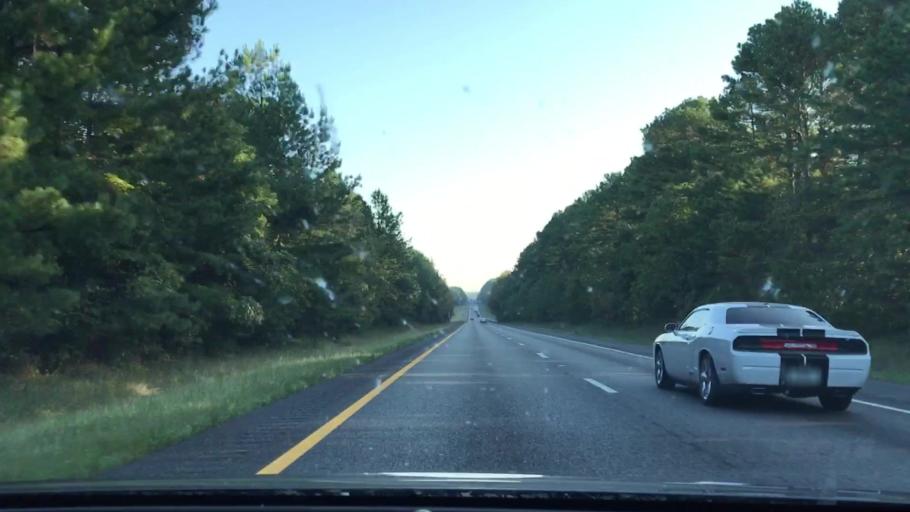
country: US
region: Tennessee
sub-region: Robertson County
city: Cross Plains
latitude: 36.5598
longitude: -86.6255
